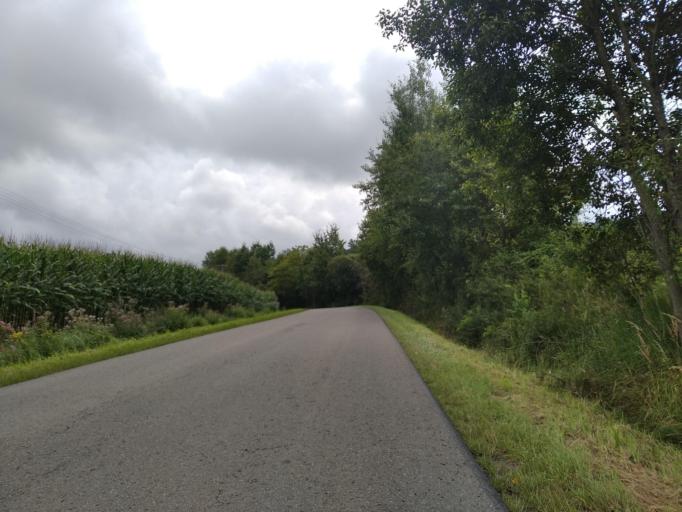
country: PL
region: Subcarpathian Voivodeship
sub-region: Powiat brzozowski
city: Nozdrzec
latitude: 49.7378
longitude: 22.2503
